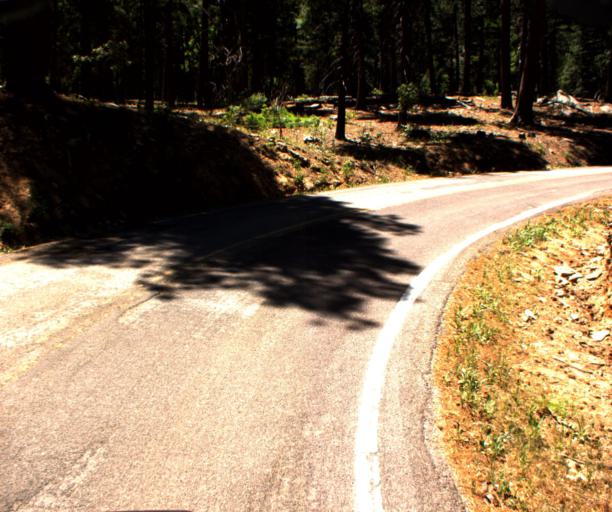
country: US
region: Arizona
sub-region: Graham County
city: Swift Trail Junction
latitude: 32.6332
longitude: -109.8167
